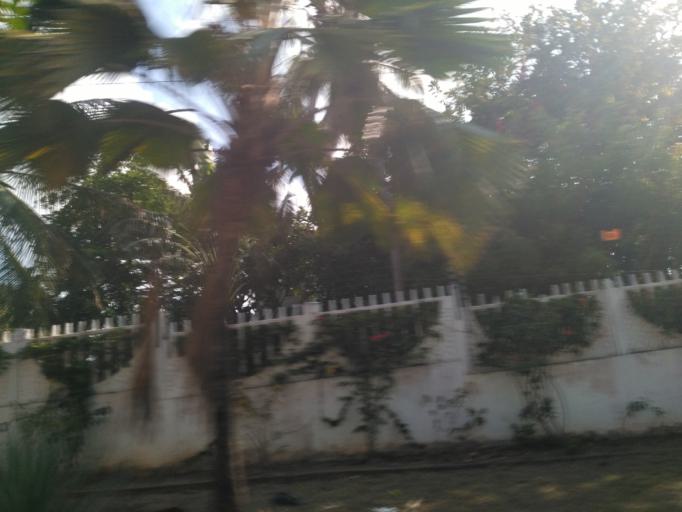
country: TZ
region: Dar es Salaam
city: Magomeni
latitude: -6.7589
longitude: 39.2842
